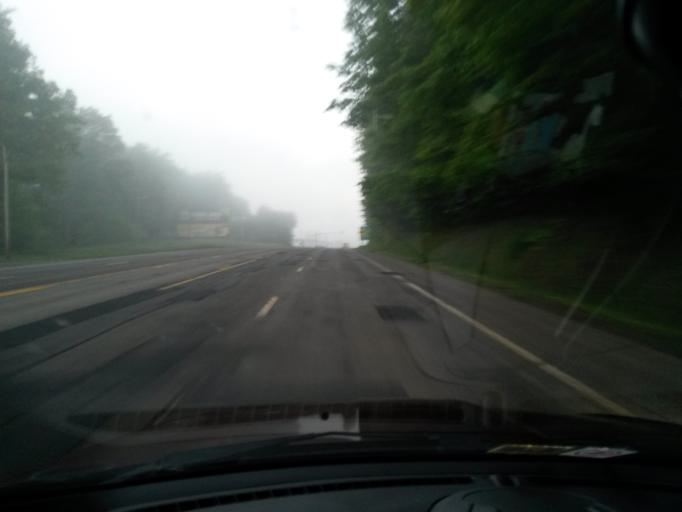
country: US
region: West Virginia
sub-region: Raleigh County
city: Crab Orchard
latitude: 37.7341
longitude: -81.2384
